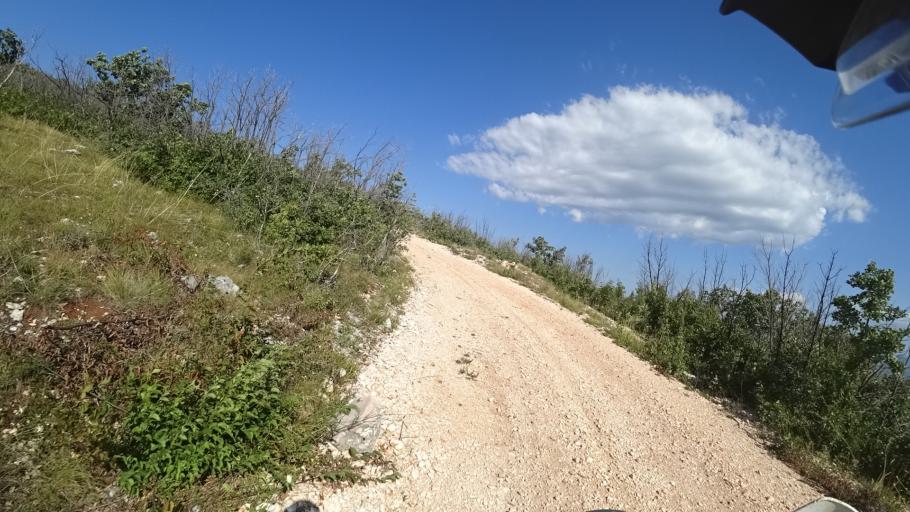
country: HR
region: Sibensko-Kniniska
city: Knin
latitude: 43.9603
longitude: 16.1575
